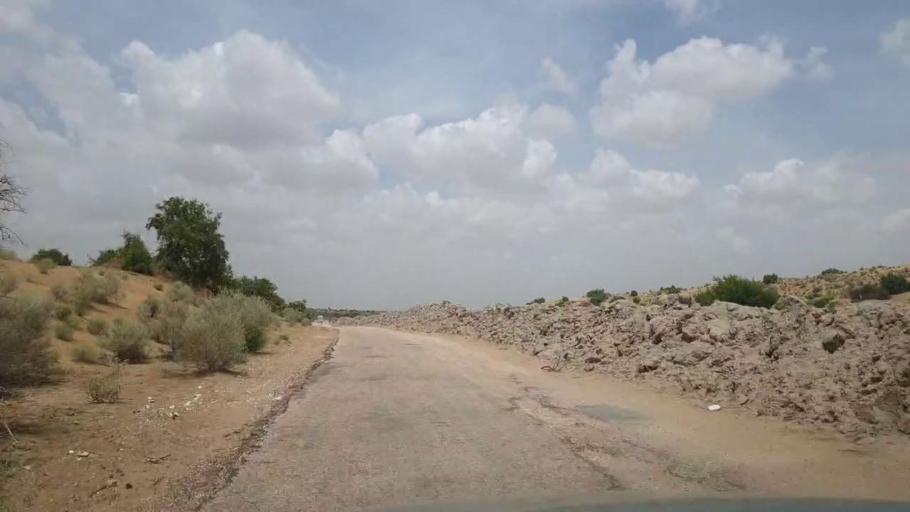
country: PK
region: Sindh
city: Kot Diji
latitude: 27.2123
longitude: 69.0982
